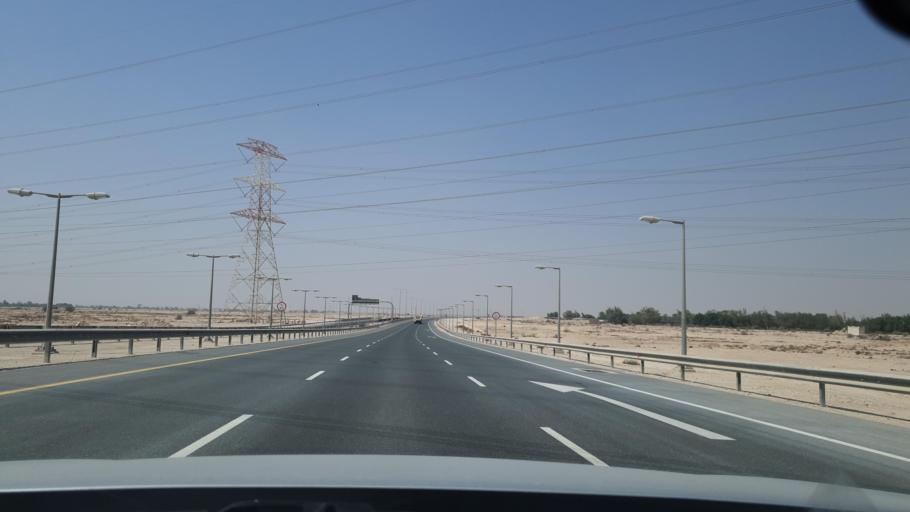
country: QA
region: Baladiyat az Za`ayin
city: Az Za`ayin
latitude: 25.6183
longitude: 51.3573
